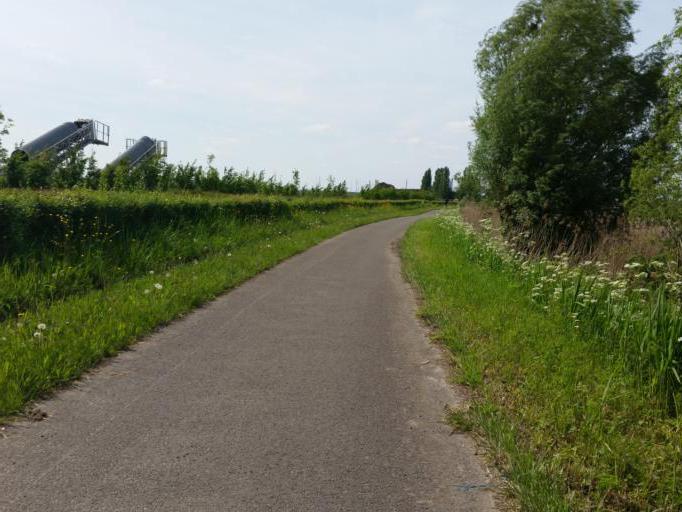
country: BE
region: Flanders
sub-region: Provincie Antwerpen
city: Niel
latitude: 51.0935
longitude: 4.3410
